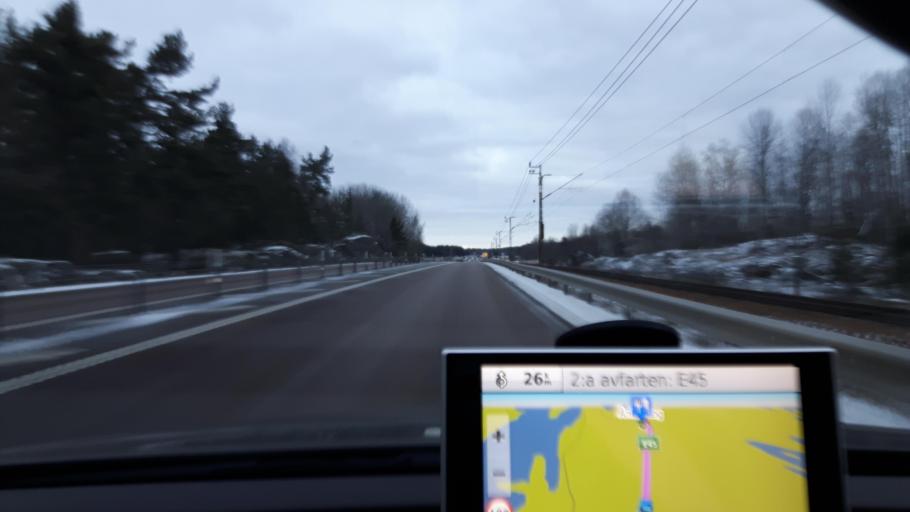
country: SE
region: Vaestra Goetaland
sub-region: Melleruds Kommun
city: Mellerud
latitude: 58.8483
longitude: 12.5522
